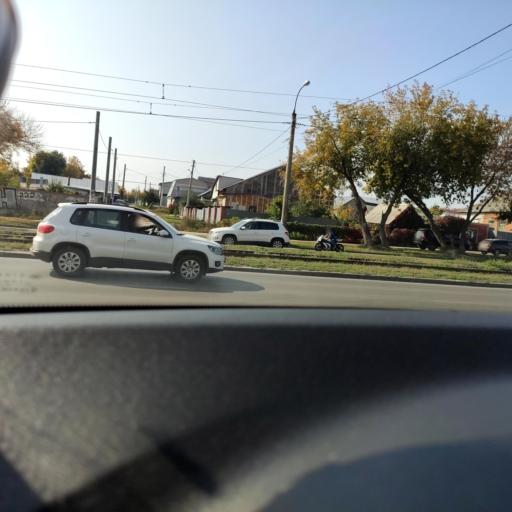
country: RU
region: Samara
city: Samara
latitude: 53.2298
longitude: 50.2278
